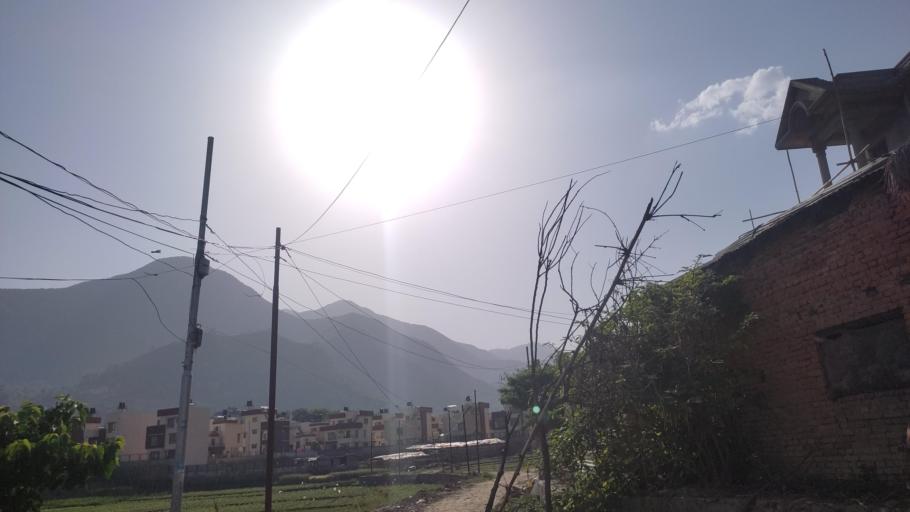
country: NP
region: Central Region
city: Kirtipur
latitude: 27.6564
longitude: 85.2841
